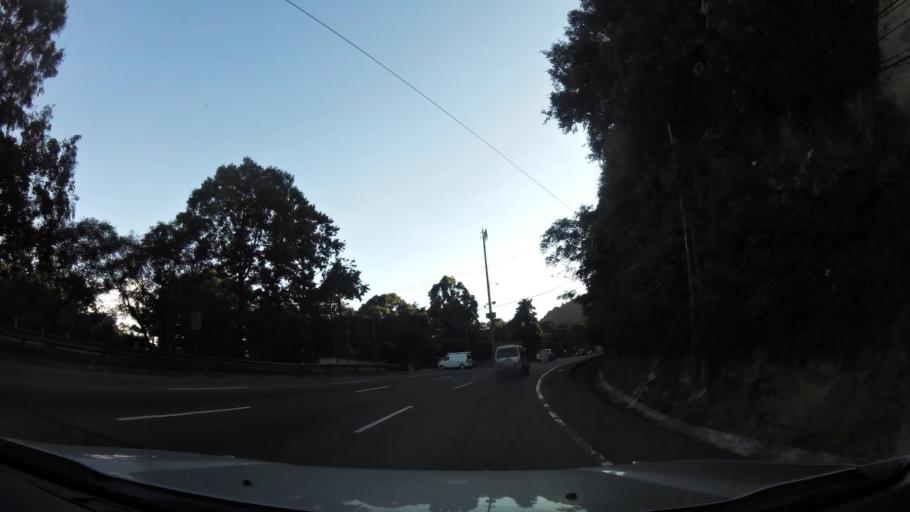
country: GT
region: Guatemala
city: Mixco
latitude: 14.6122
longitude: -90.6220
